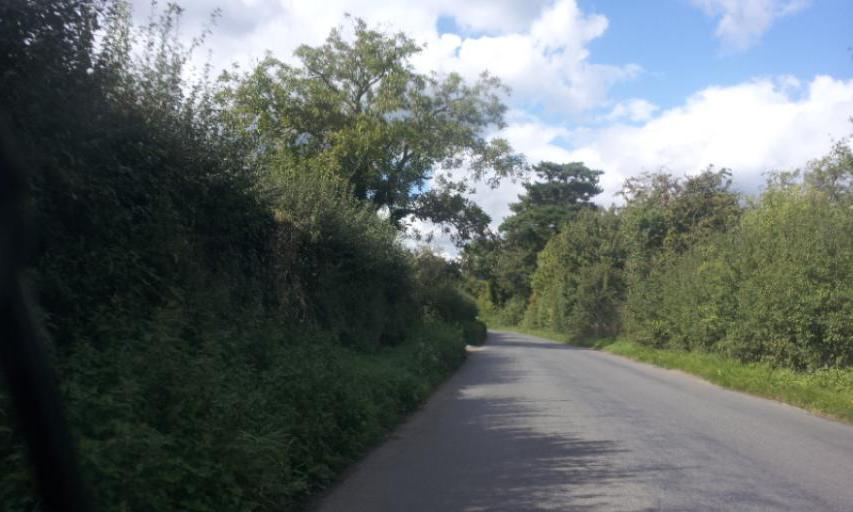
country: GB
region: England
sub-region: Kent
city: West Malling
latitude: 51.3157
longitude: 0.4135
